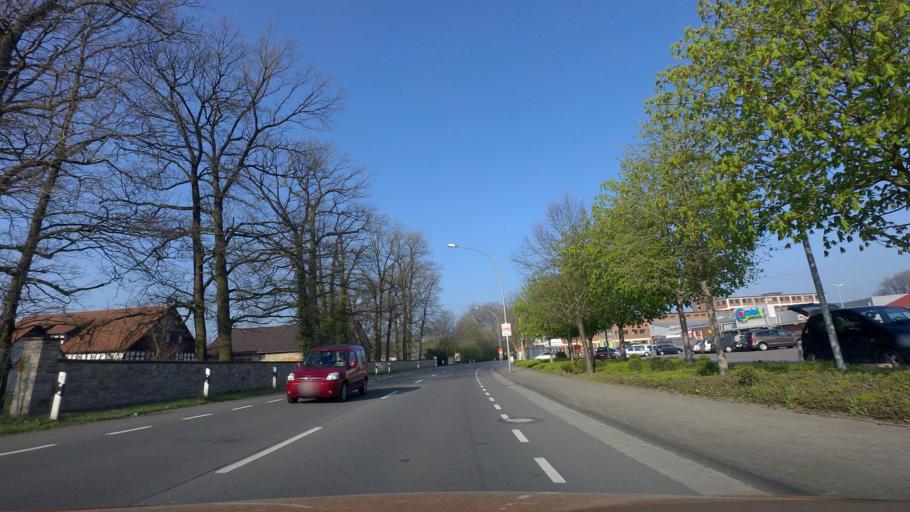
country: DE
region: Lower Saxony
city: Melle
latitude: 52.2090
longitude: 8.3329
